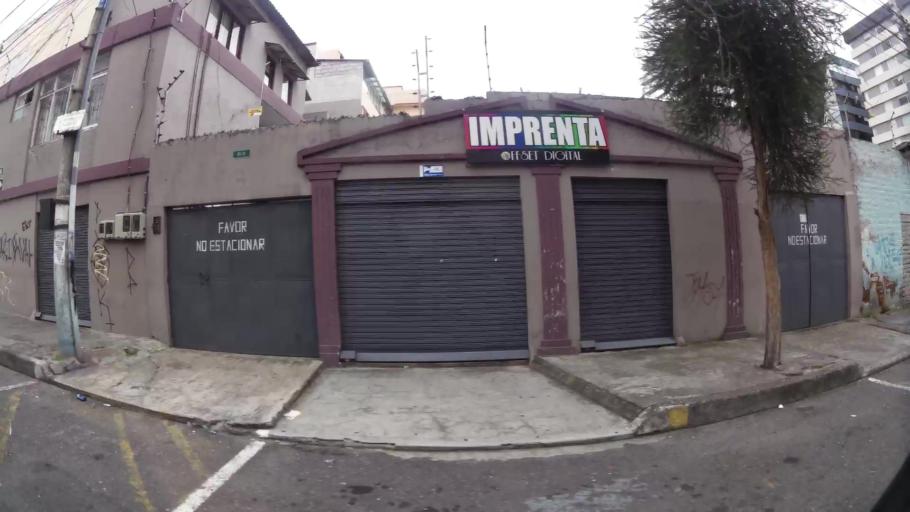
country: EC
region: Pichincha
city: Quito
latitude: -0.1770
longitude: -78.4883
